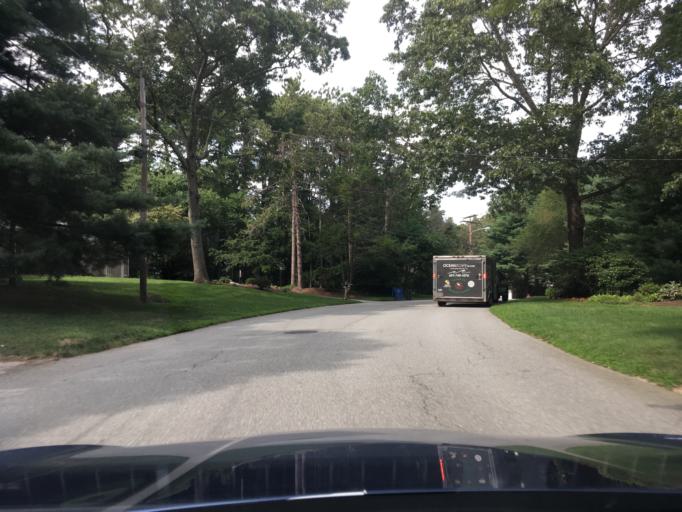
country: US
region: Rhode Island
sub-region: Kent County
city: East Greenwich
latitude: 41.6481
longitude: -71.4860
